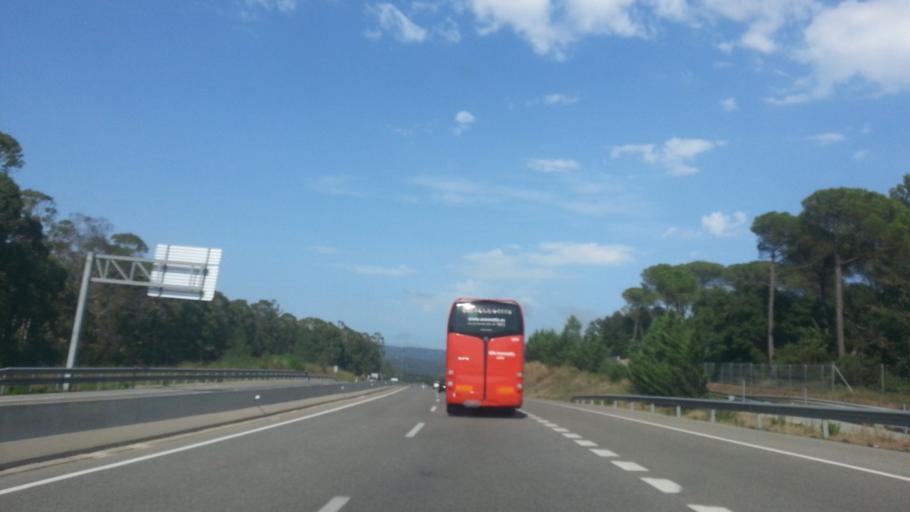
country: ES
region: Catalonia
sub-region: Provincia de Girona
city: Llagostera
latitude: 41.8217
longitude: 2.9081
